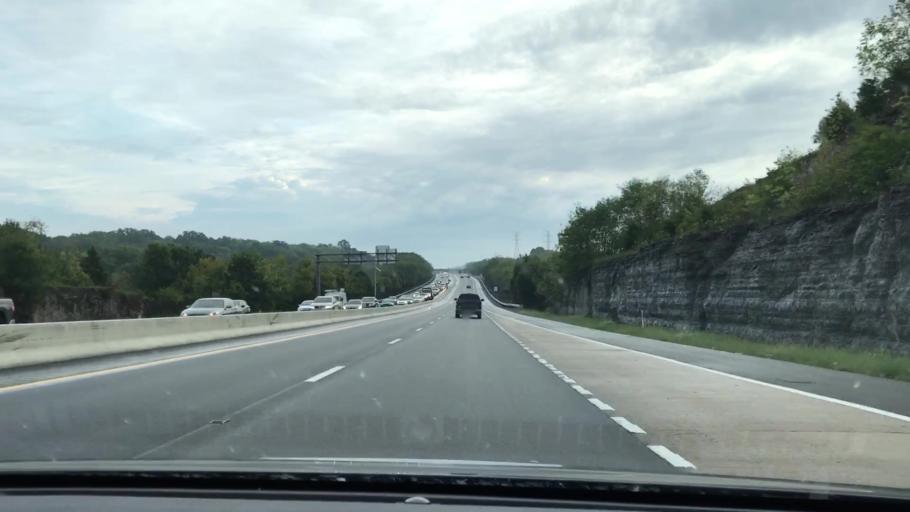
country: US
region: Tennessee
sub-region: Sumner County
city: Hendersonville
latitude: 36.3155
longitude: -86.6504
